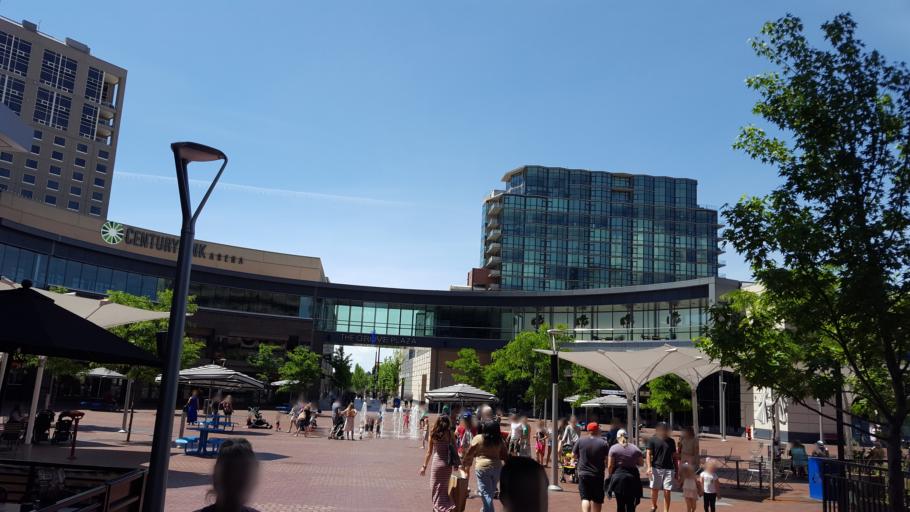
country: US
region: Idaho
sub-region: Ada County
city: Boise
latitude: 43.6153
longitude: -116.2039
